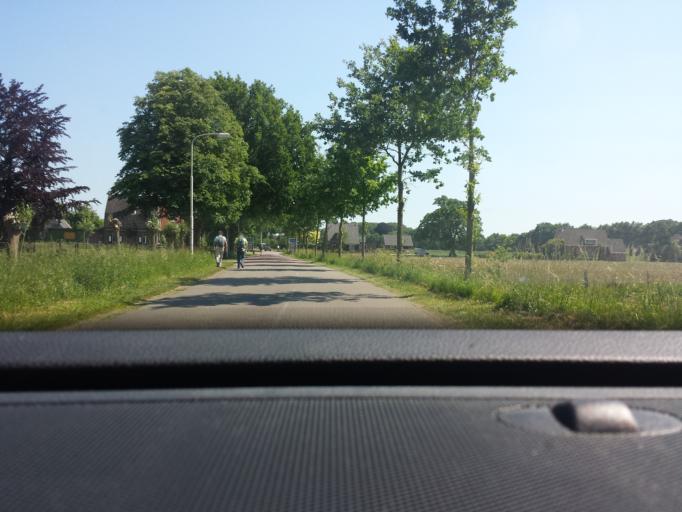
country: NL
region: Gelderland
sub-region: Gemeente Lochem
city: Almen
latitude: 52.1121
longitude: 6.3121
